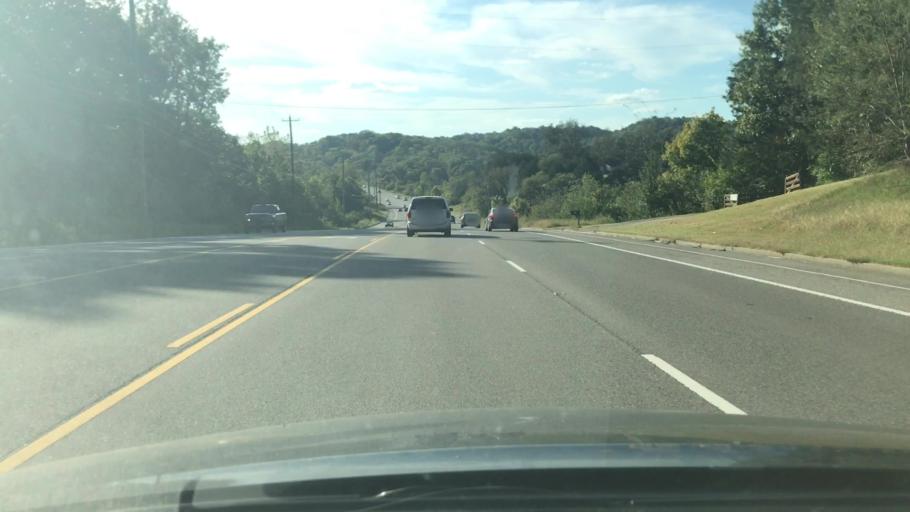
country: US
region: Tennessee
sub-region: Davidson County
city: Nashville
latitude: 36.2108
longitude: -86.8859
